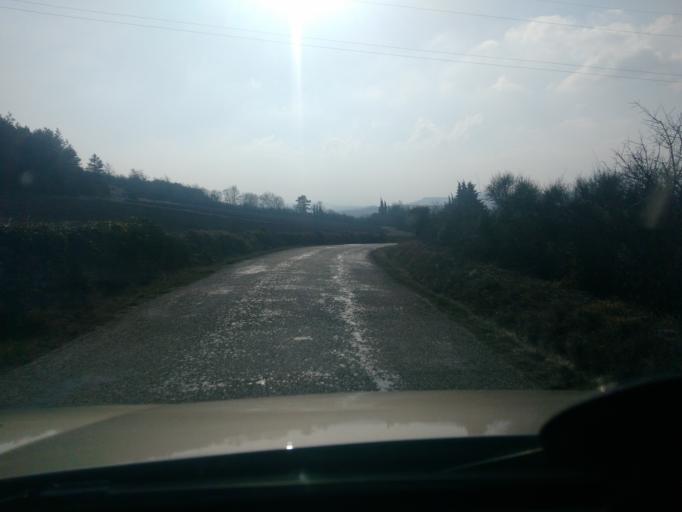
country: FR
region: Rhone-Alpes
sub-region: Departement de la Drome
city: Allan
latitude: 44.4782
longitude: 4.8585
